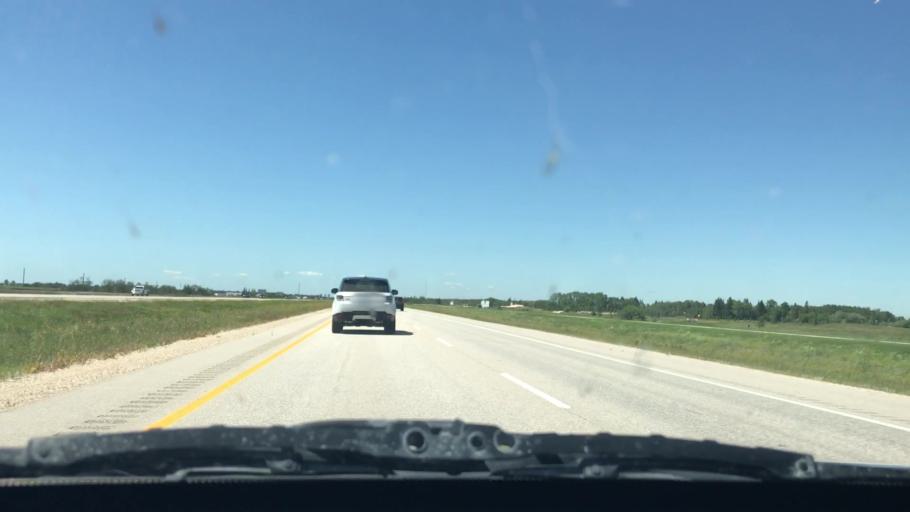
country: CA
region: Manitoba
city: Niverville
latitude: 49.8070
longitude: -96.9036
